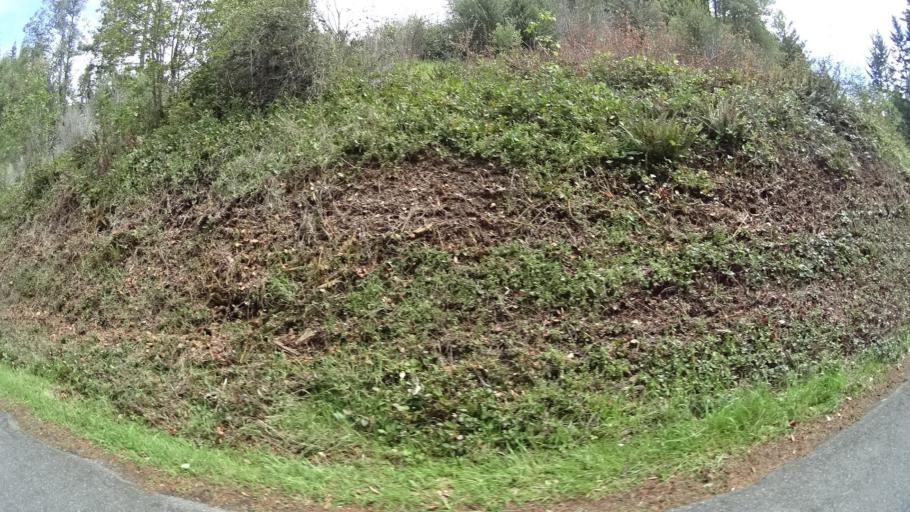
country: US
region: California
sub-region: Humboldt County
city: Blue Lake
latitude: 40.7931
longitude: -123.9759
